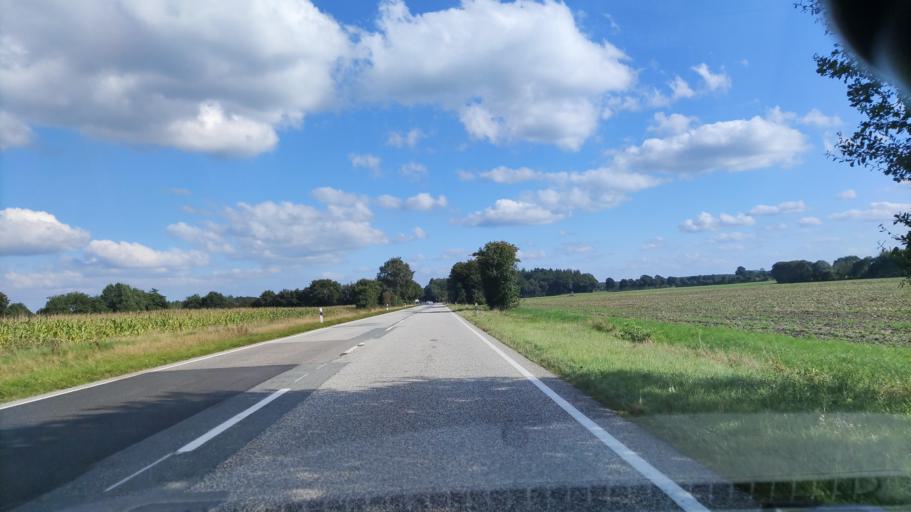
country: DE
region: Schleswig-Holstein
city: Jevenstedt
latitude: 54.2261
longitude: 9.6964
